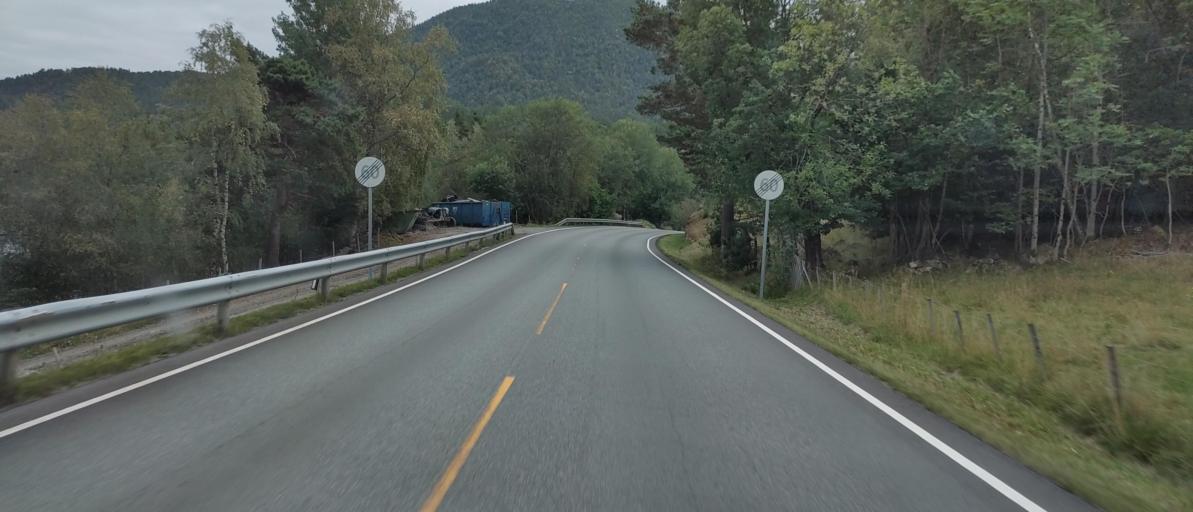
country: NO
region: More og Romsdal
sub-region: Rauma
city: Andalsnes
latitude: 62.5792
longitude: 7.5495
